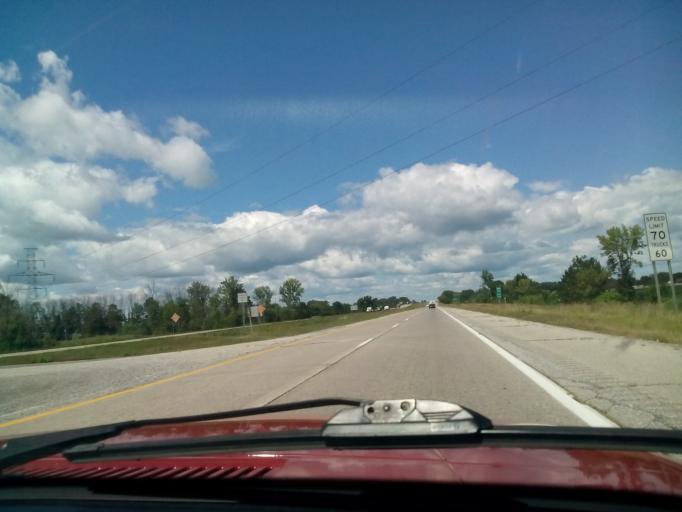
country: US
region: Michigan
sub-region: Bay County
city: Bay City
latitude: 43.6311
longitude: -83.9632
